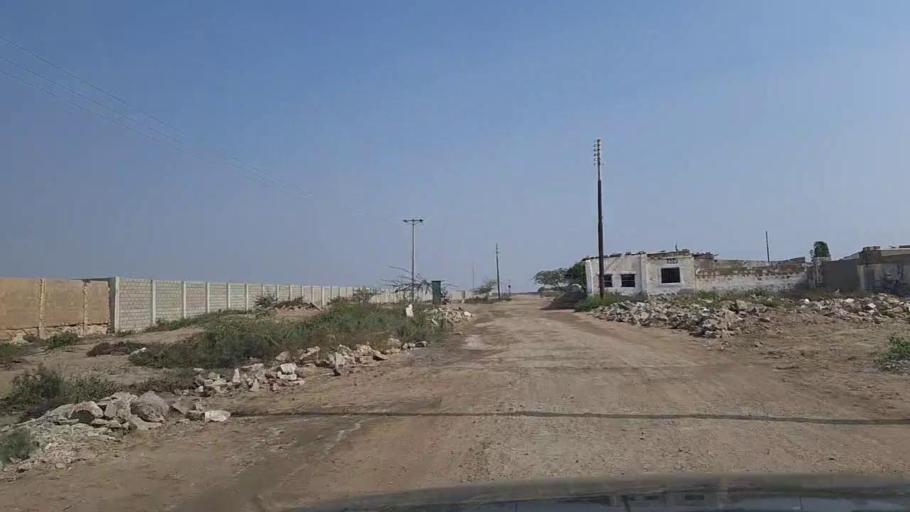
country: PK
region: Sindh
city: Gharo
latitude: 24.7392
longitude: 67.6167
